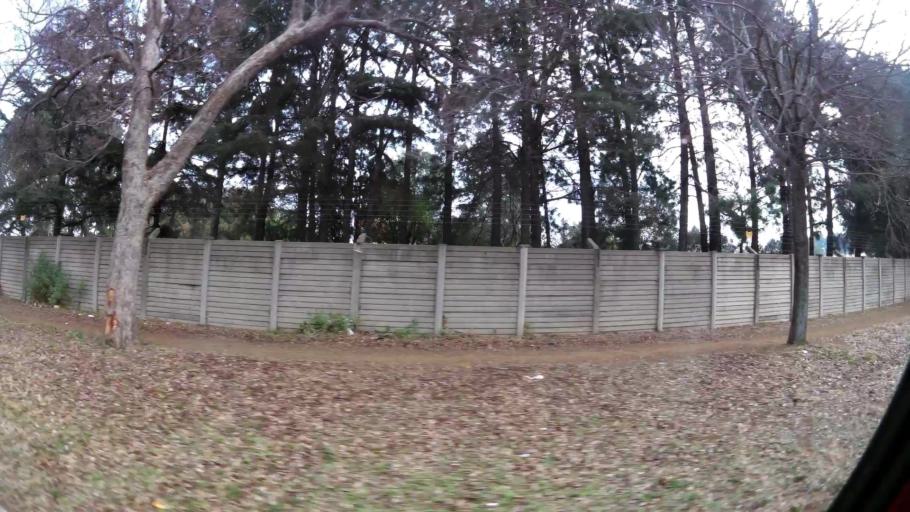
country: ZA
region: Gauteng
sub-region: Sedibeng District Municipality
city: Vanderbijlpark
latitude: -26.6880
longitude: 27.8260
